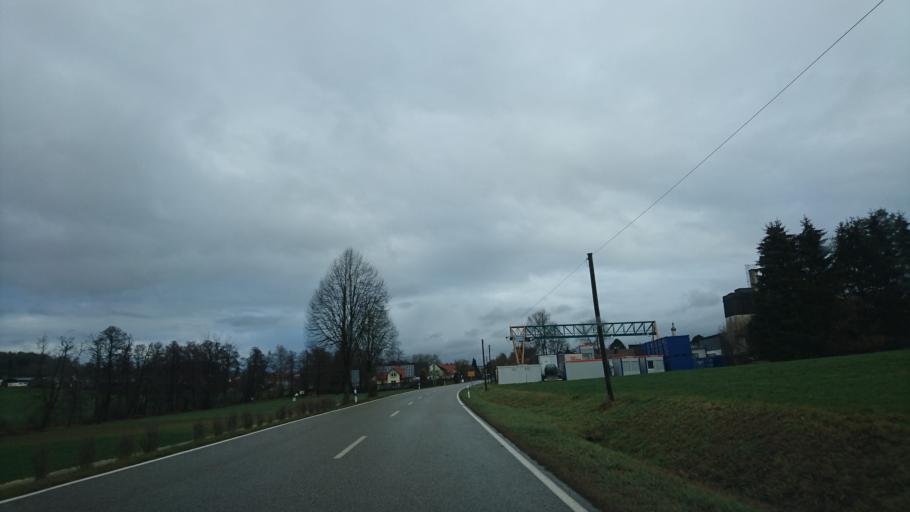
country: DE
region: Bavaria
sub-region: Swabia
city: Biberbach
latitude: 48.5110
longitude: 10.8028
